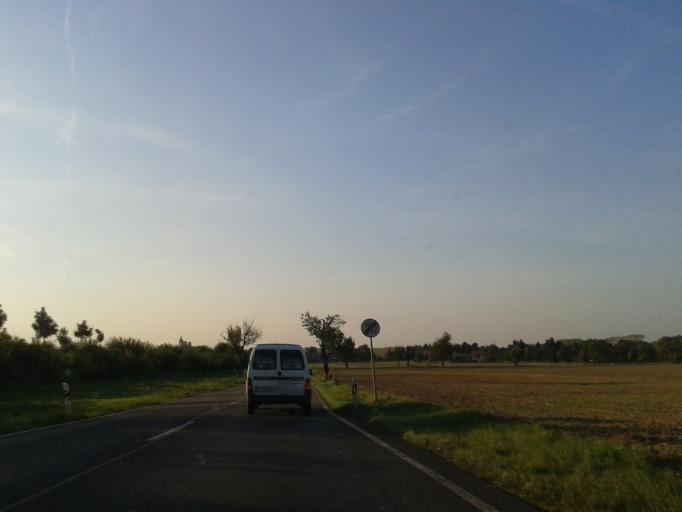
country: DE
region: Saxony
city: Klipphausen
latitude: 51.0723
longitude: 13.5122
